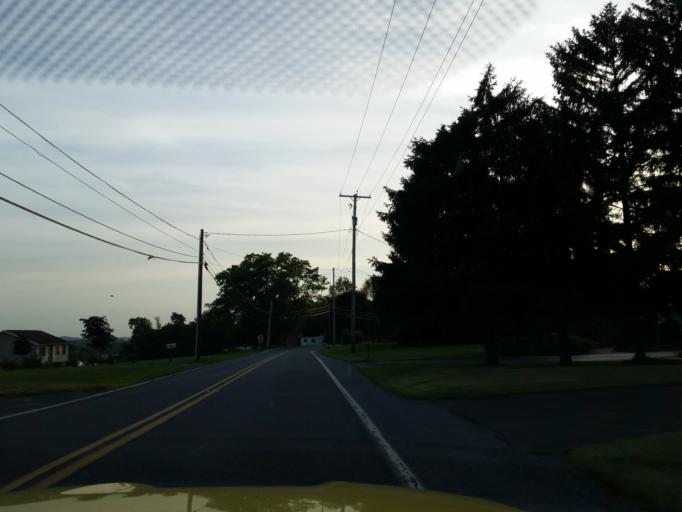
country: US
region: Pennsylvania
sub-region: Lebanon County
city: Fredericksburg
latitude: 40.4473
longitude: -76.3699
